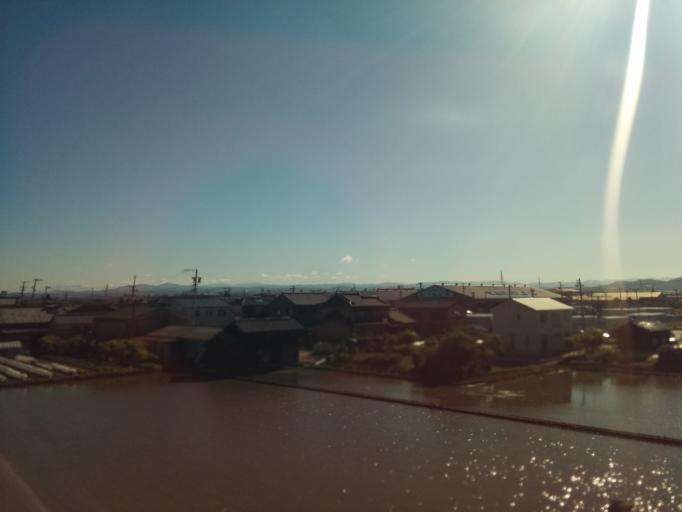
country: JP
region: Aichi
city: Okazaki
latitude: 34.9037
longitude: 137.1206
